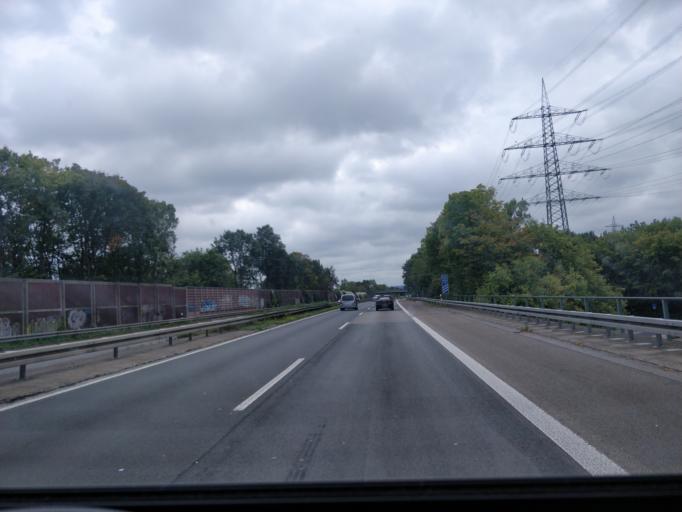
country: DE
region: North Rhine-Westphalia
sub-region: Regierungsbezirk Koln
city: Troisdorf
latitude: 50.8131
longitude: 7.1228
